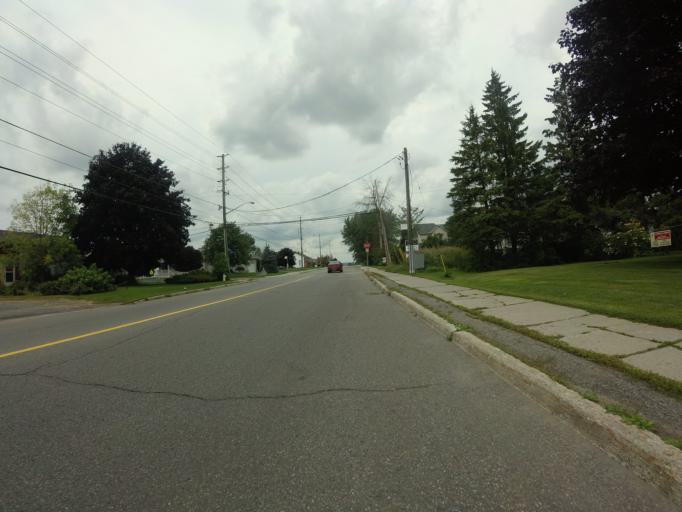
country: CA
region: Quebec
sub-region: Outaouais
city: Gatineau
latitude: 45.4671
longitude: -75.5191
